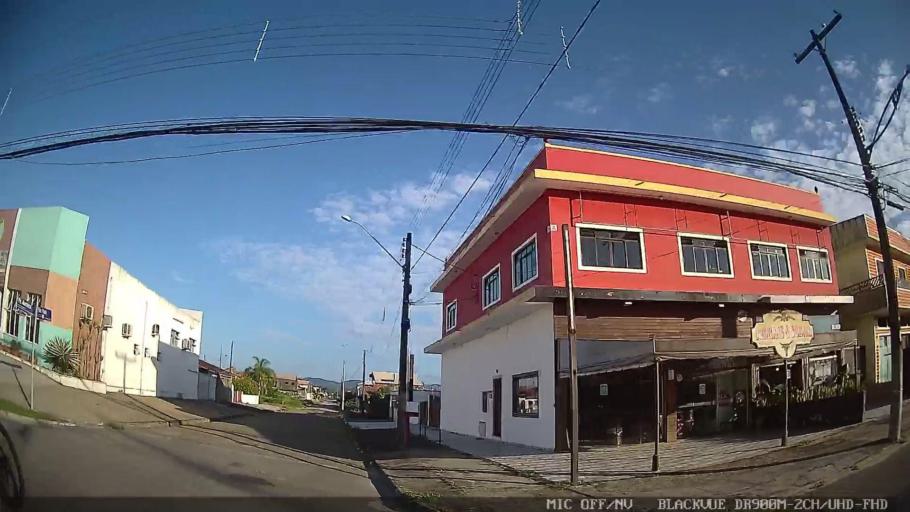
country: BR
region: Sao Paulo
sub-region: Peruibe
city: Peruibe
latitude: -24.2871
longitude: -46.9577
